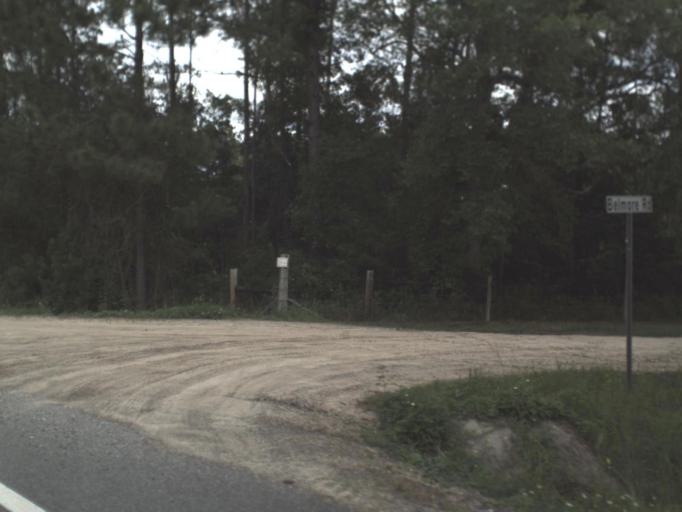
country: US
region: Florida
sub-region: Clay County
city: Keystone Heights
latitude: 29.8967
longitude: -81.9030
